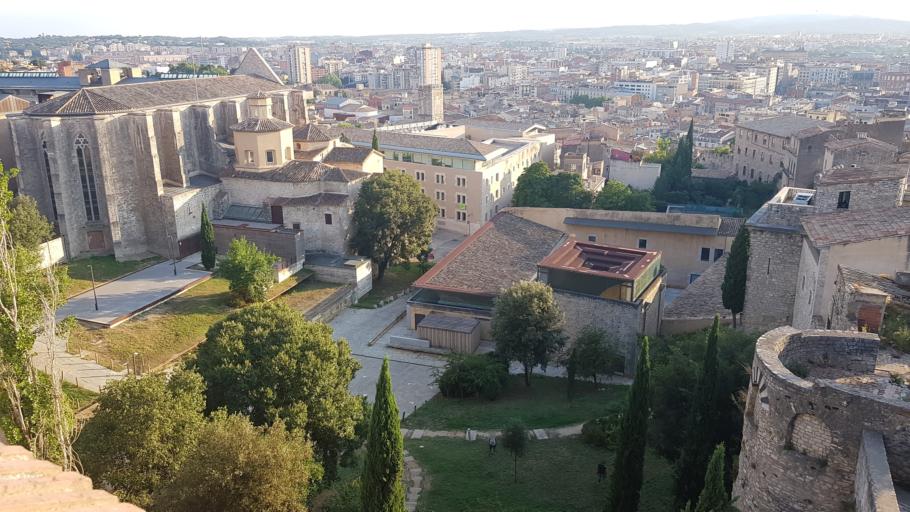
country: ES
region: Catalonia
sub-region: Provincia de Girona
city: Girona
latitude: 41.9866
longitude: 2.8284
